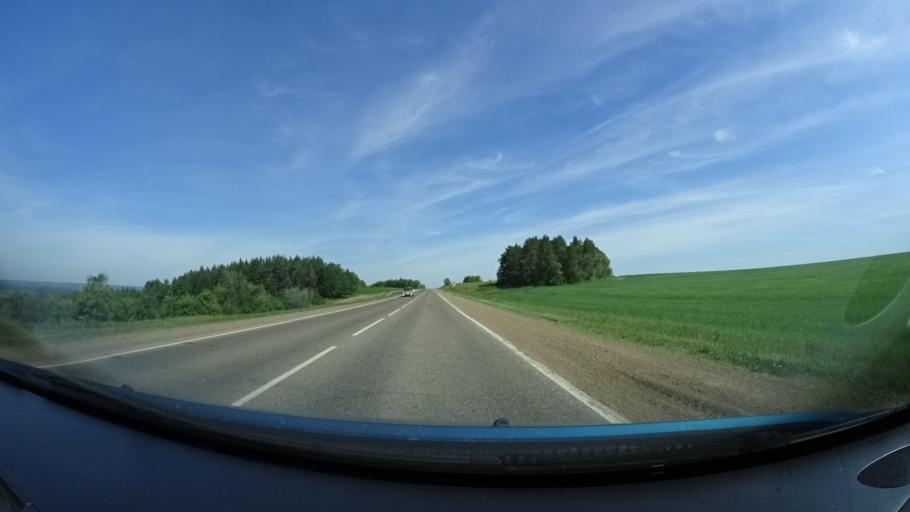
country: RU
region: Bashkortostan
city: Blagoveshchensk
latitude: 55.1529
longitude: 55.8528
